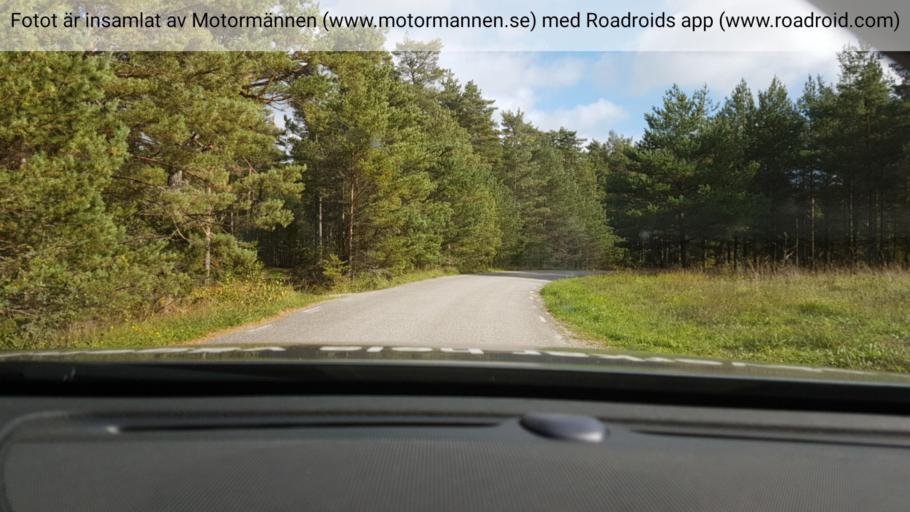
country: SE
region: Gotland
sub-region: Gotland
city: Slite
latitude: 57.9646
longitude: 19.2986
